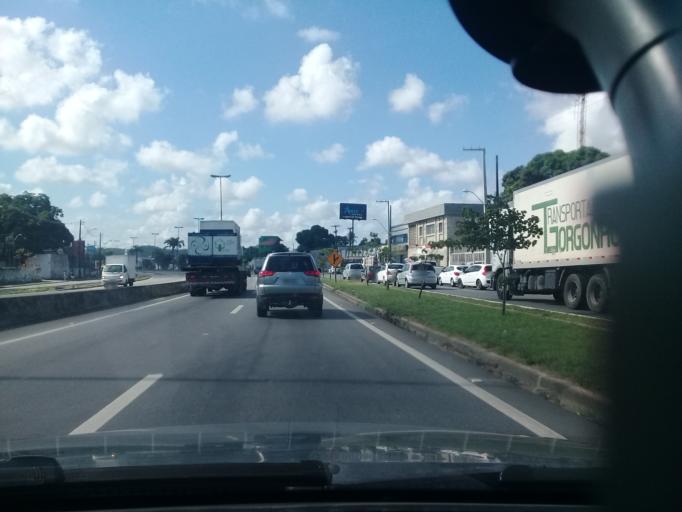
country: BR
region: Pernambuco
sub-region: Recife
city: Recife
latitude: -8.0372
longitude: -34.9415
